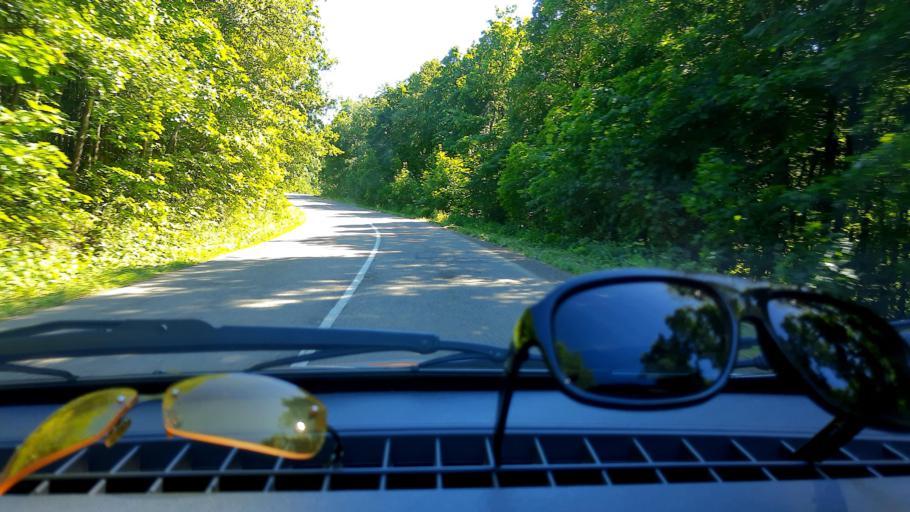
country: RU
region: Bashkortostan
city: Ulu-Telyak
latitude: 54.8144
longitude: 57.0370
